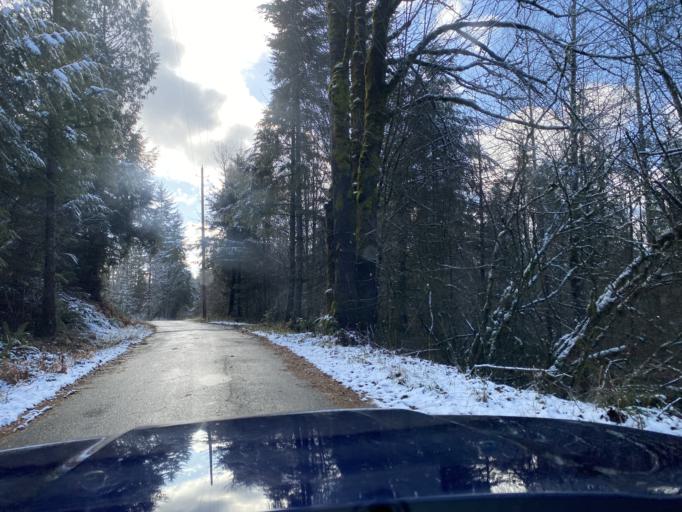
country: US
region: Washington
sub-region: King County
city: Snoqualmie
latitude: 47.5016
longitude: -121.8778
